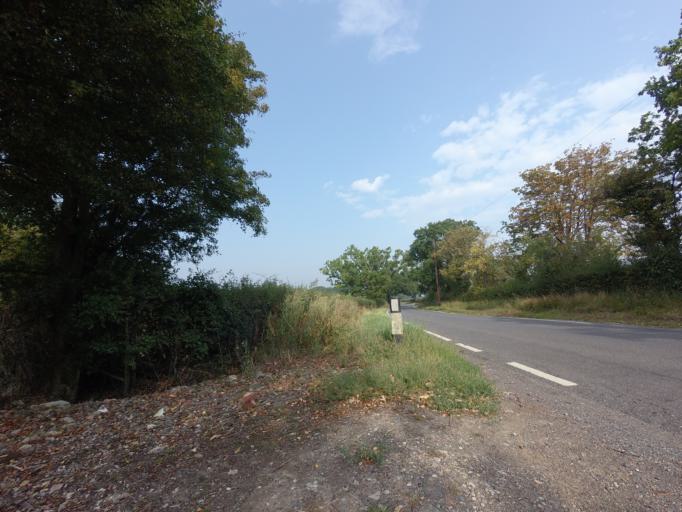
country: GB
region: England
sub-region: Kent
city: Tenterden
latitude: 51.1191
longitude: 0.6989
